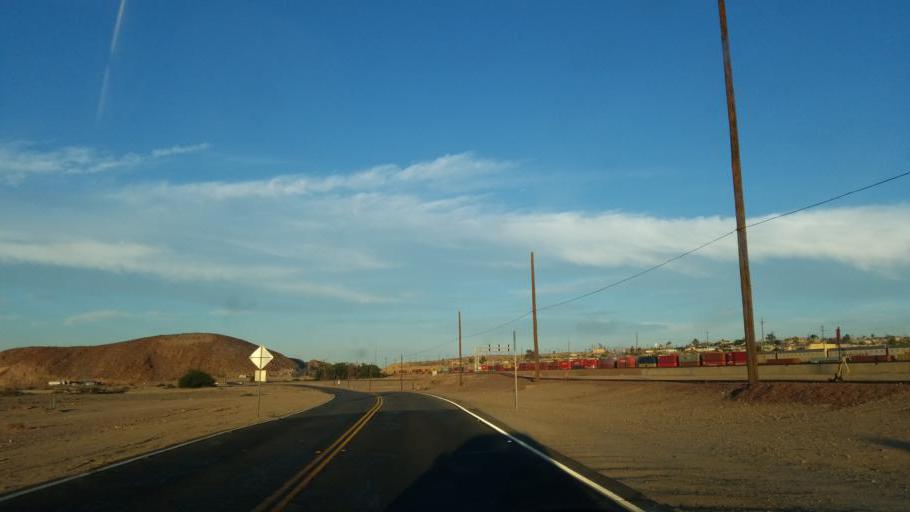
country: US
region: California
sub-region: San Bernardino County
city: Barstow
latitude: 34.9046
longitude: -117.0213
